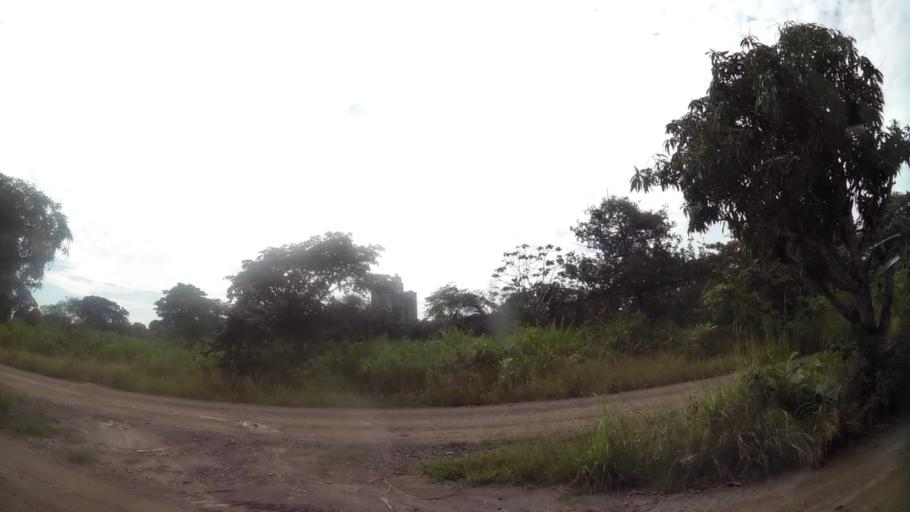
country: PA
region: Panama
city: Nueva Gorgona
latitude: 8.5466
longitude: -79.8880
